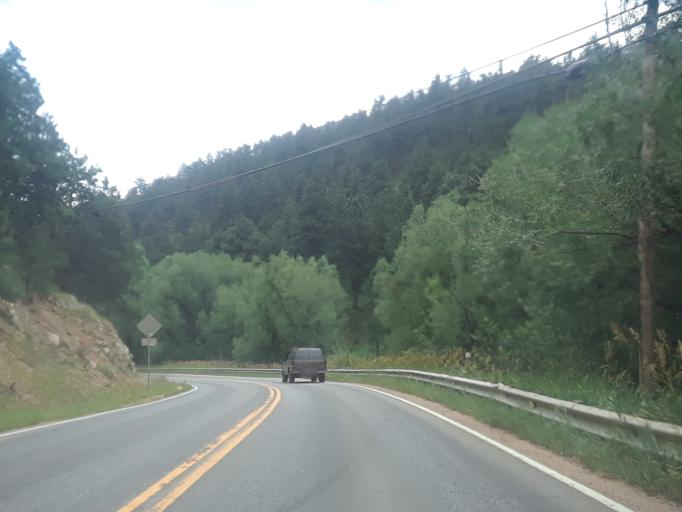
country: US
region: Colorado
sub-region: Boulder County
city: Boulder
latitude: 40.0264
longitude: -105.3131
